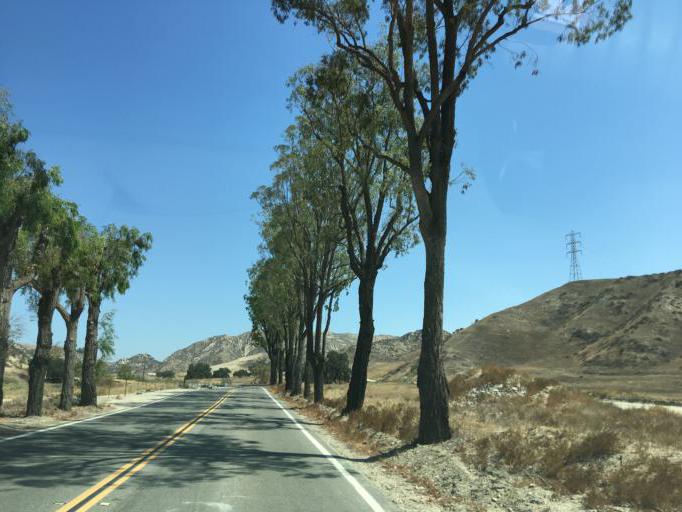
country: US
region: California
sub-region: Los Angeles County
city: Val Verde
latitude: 34.4226
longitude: -118.6572
